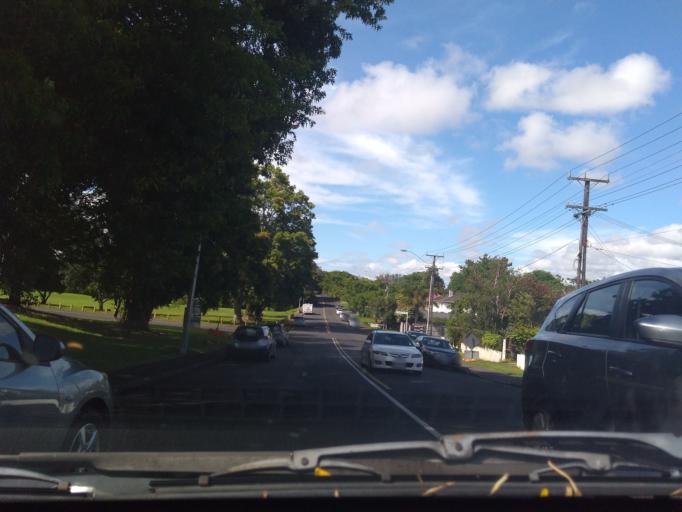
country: NZ
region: Auckland
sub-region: Auckland
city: Auckland
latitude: -36.8717
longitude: 174.7270
